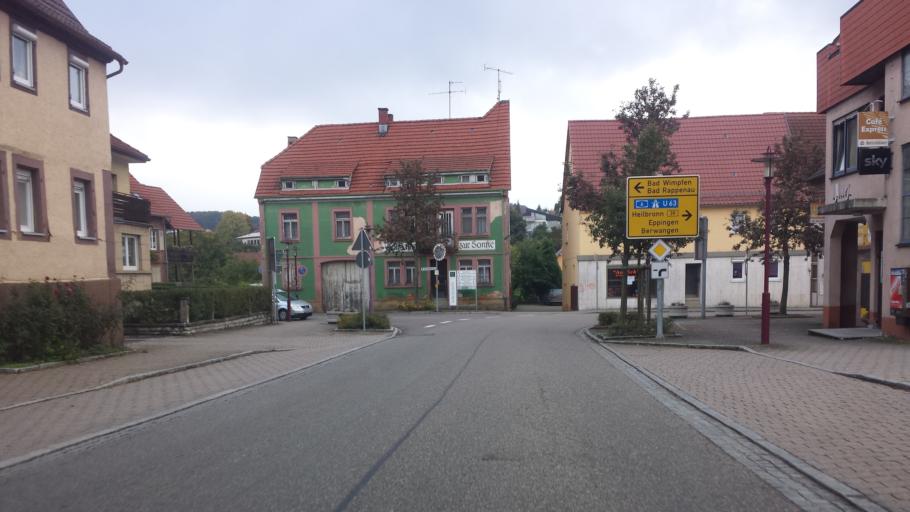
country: DE
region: Baden-Wuerttemberg
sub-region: Regierungsbezirk Stuttgart
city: Kirchardt
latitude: 49.2072
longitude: 8.9914
